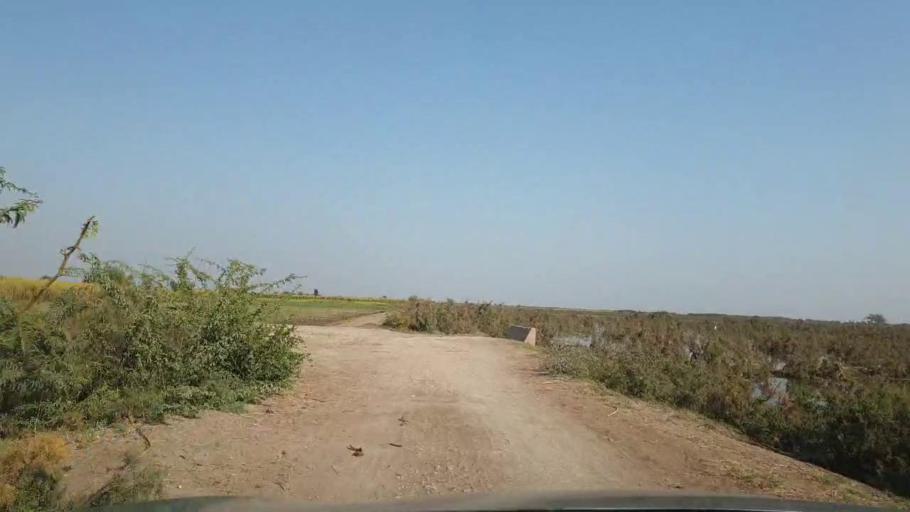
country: PK
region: Sindh
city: Berani
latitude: 25.6427
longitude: 68.8260
